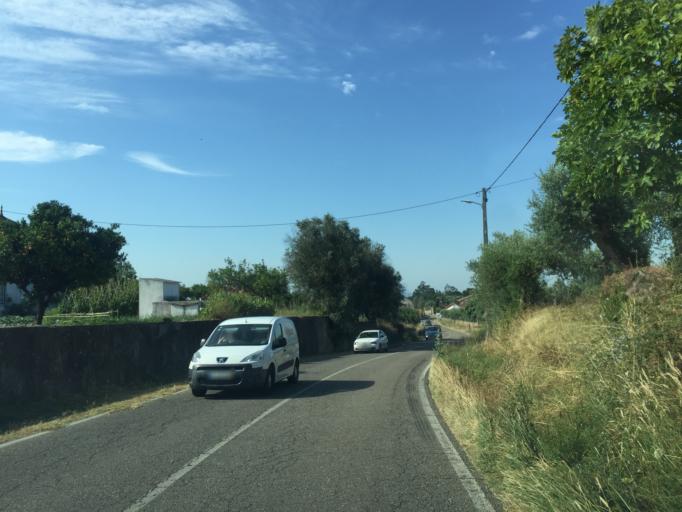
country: PT
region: Santarem
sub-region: Tomar
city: Tomar
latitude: 39.6568
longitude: -8.3700
